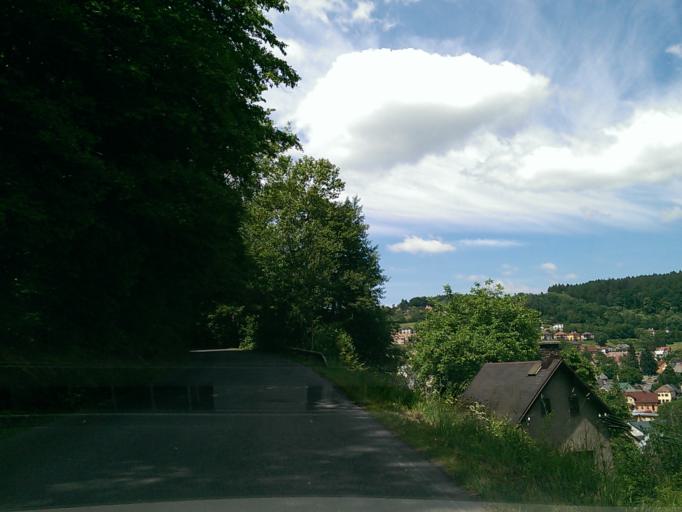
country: CZ
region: Liberecky
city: Zelezny Brod
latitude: 50.6394
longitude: 15.2589
